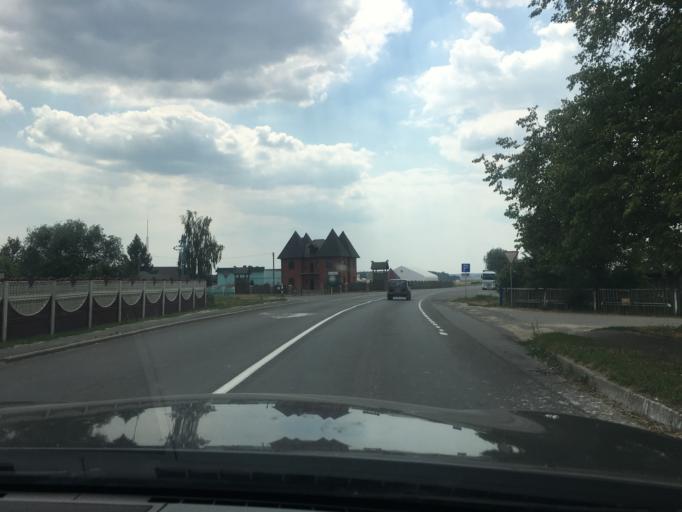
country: BY
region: Brest
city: Ruzhany
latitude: 52.8600
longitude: 24.8900
